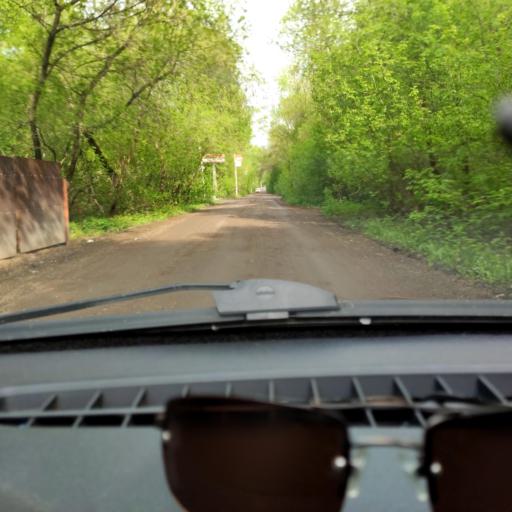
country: RU
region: Bashkortostan
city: Ufa
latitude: 54.6985
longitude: 55.9344
